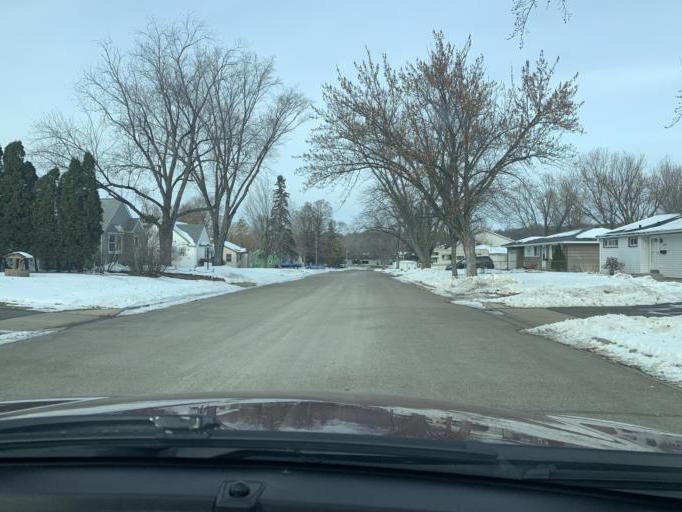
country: US
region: Minnesota
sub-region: Washington County
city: Saint Paul Park
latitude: 44.8375
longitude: -92.9770
